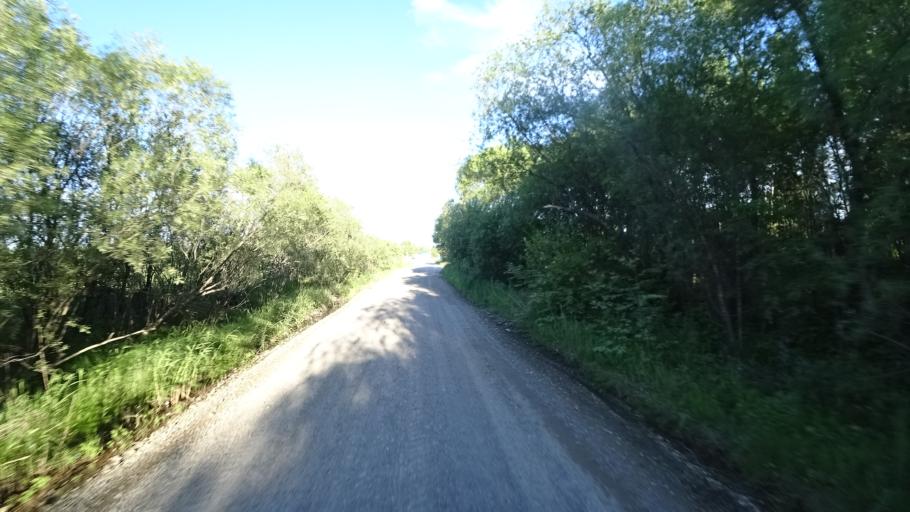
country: RU
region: Khabarovsk Krai
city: Khor
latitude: 47.8427
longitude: 134.9542
